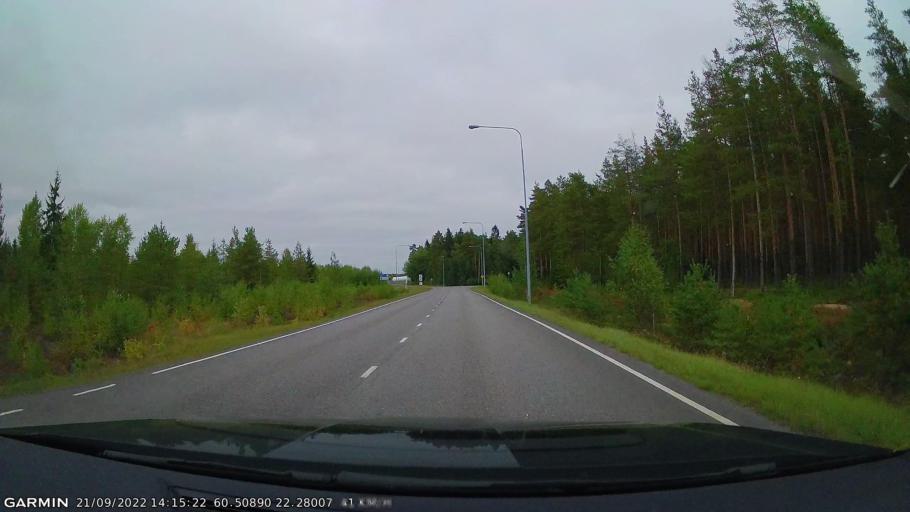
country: FI
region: Varsinais-Suomi
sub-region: Turku
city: Turku
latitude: 60.5090
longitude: 22.2802
